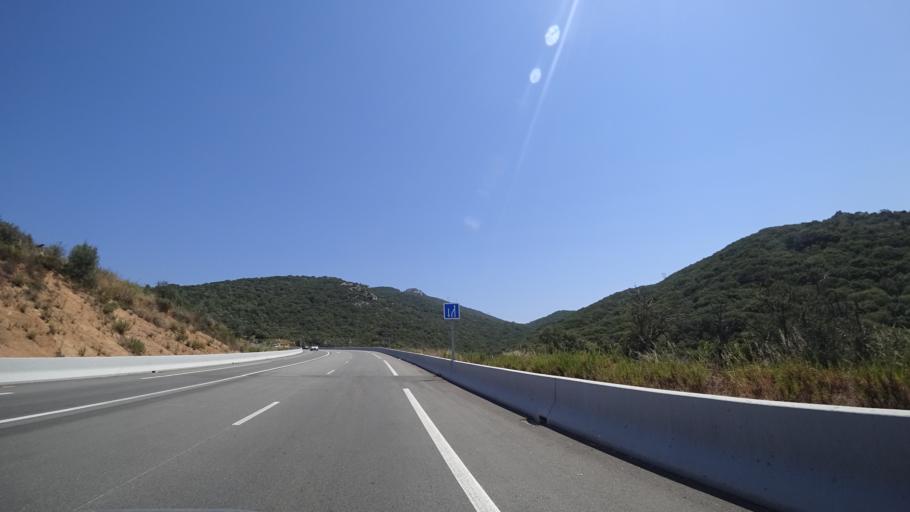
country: FR
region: Corsica
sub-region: Departement de la Corse-du-Sud
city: Propriano
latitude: 41.6679
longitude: 8.9243
